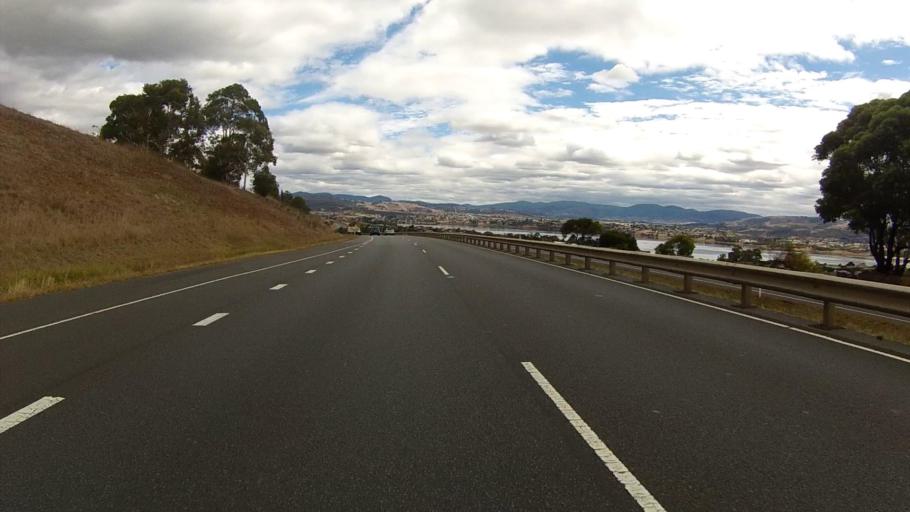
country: AU
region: Tasmania
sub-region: Glenorchy
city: Austins Ferry
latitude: -42.7733
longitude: 147.2388
